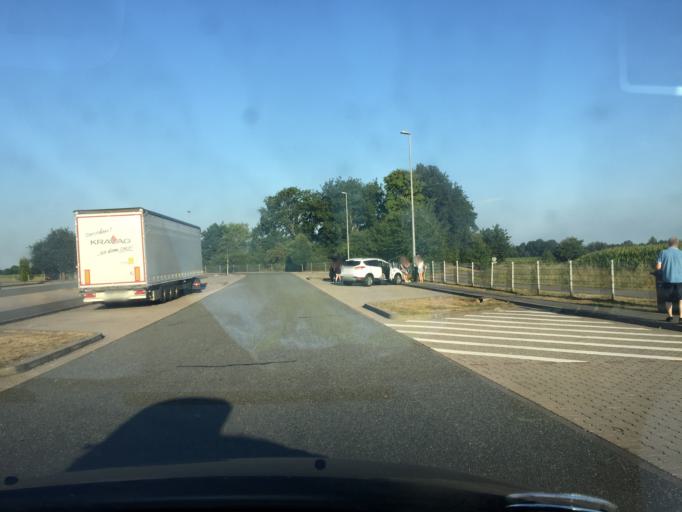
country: DE
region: Schleswig-Holstein
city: Wasbek
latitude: 54.0927
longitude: 9.9297
